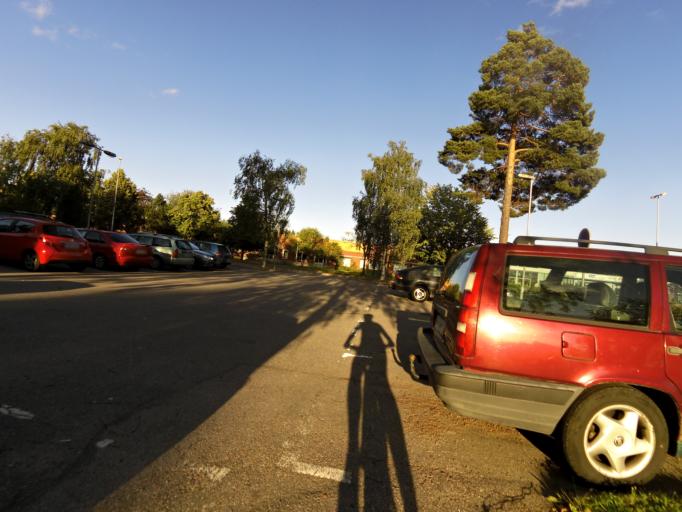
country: SE
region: Gaevleborg
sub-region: Gavle Kommun
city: Gavle
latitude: 60.6517
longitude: 17.1370
